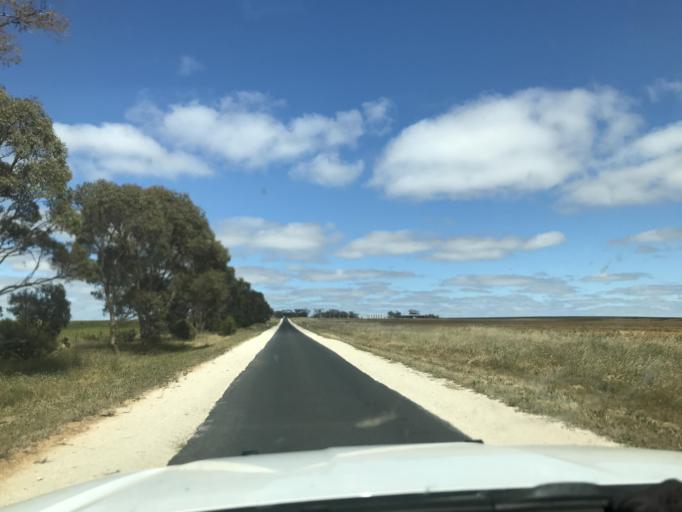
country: AU
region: South Australia
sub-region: Tatiara
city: Bordertown
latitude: -36.3059
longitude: 141.0887
